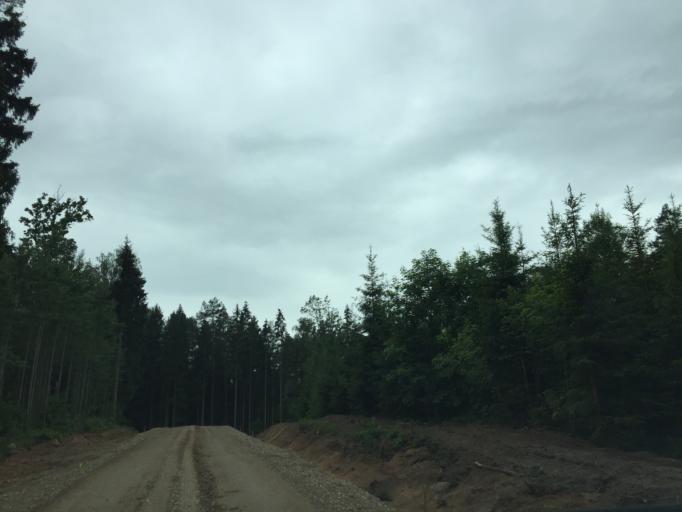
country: LV
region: Tukuma Rajons
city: Tukums
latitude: 57.0042
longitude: 23.1122
